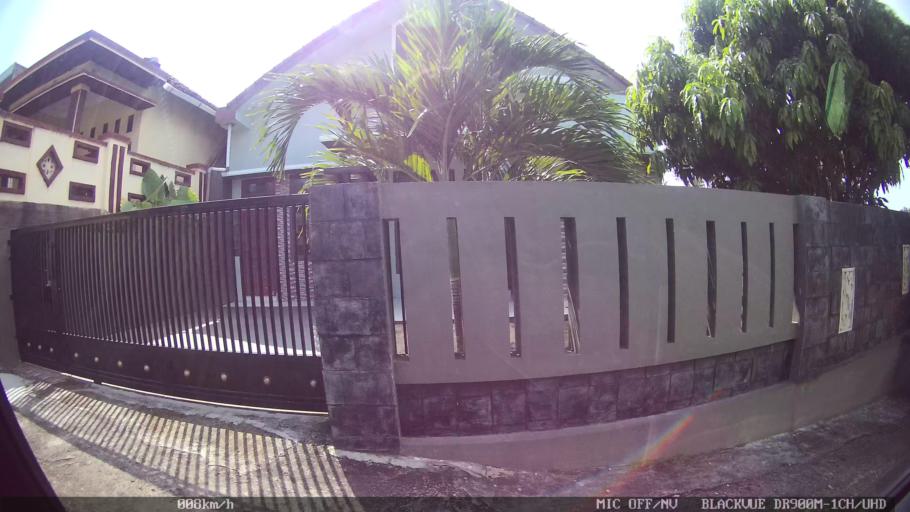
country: ID
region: Lampung
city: Kedaton
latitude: -5.4011
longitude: 105.2383
